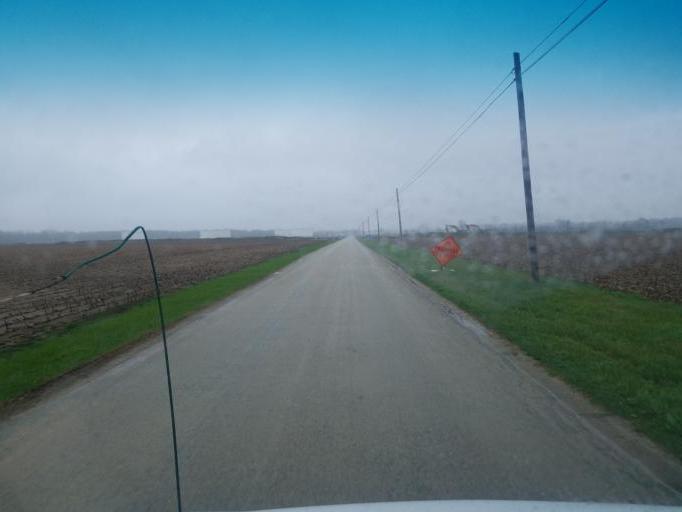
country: US
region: Ohio
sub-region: Wood County
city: North Baltimore
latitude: 41.2363
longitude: -83.6403
